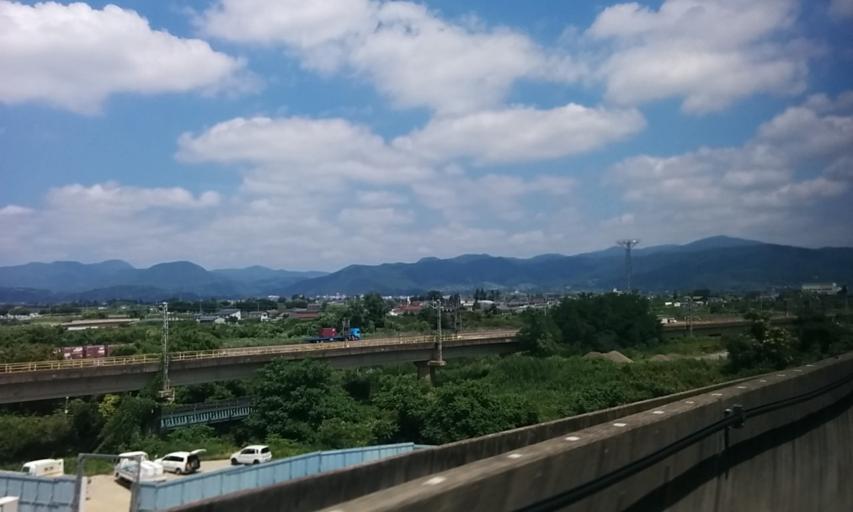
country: JP
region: Fukushima
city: Fukushima-shi
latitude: 37.7929
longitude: 140.4736
